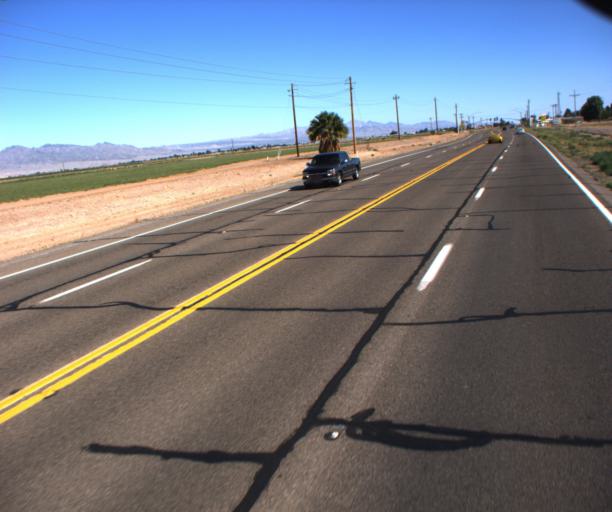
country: US
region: Arizona
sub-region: Mohave County
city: Willow Valley
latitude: 34.8919
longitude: -114.5977
